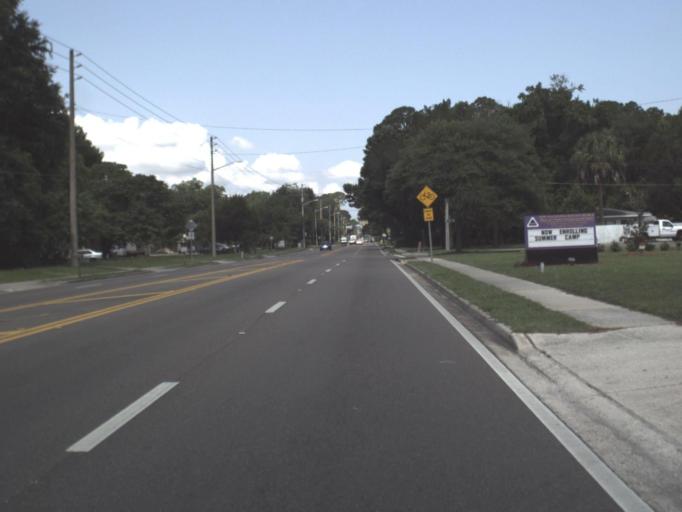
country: US
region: Florida
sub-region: Alachua County
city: Gainesville
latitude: 29.6739
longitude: -82.3067
